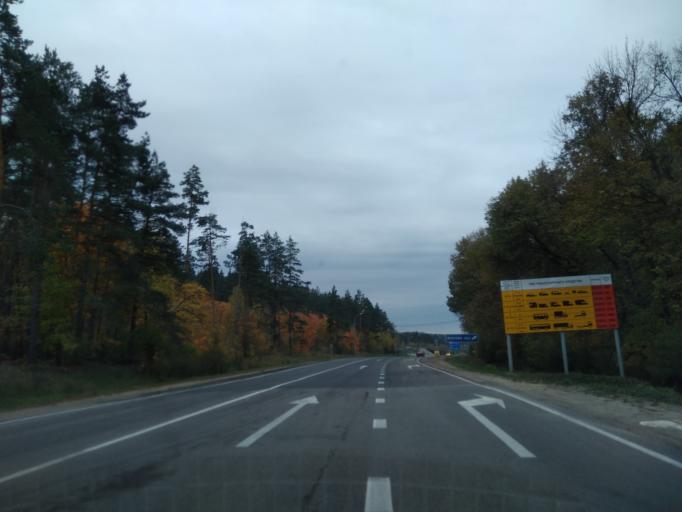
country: RU
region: Lipetsk
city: Zadonsk
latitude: 52.3731
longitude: 38.9183
